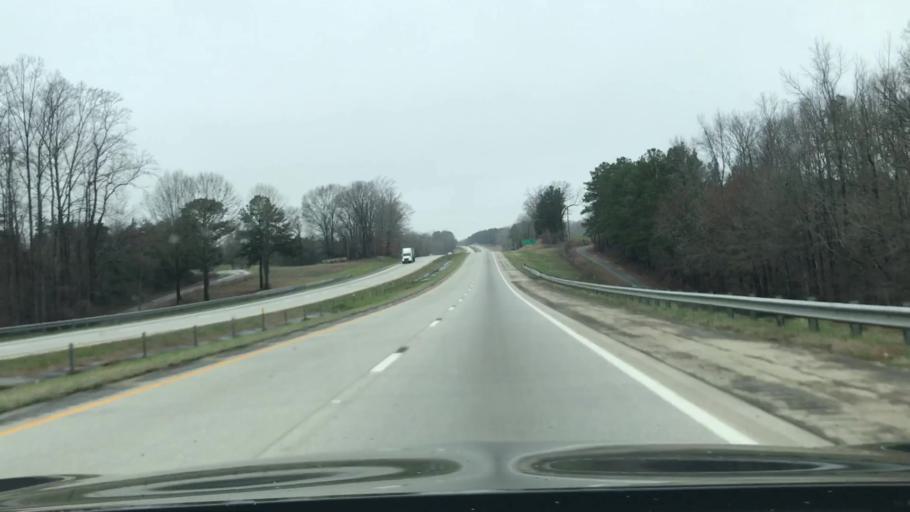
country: US
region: South Carolina
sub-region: Laurens County
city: Clinton
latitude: 34.5204
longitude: -81.9094
